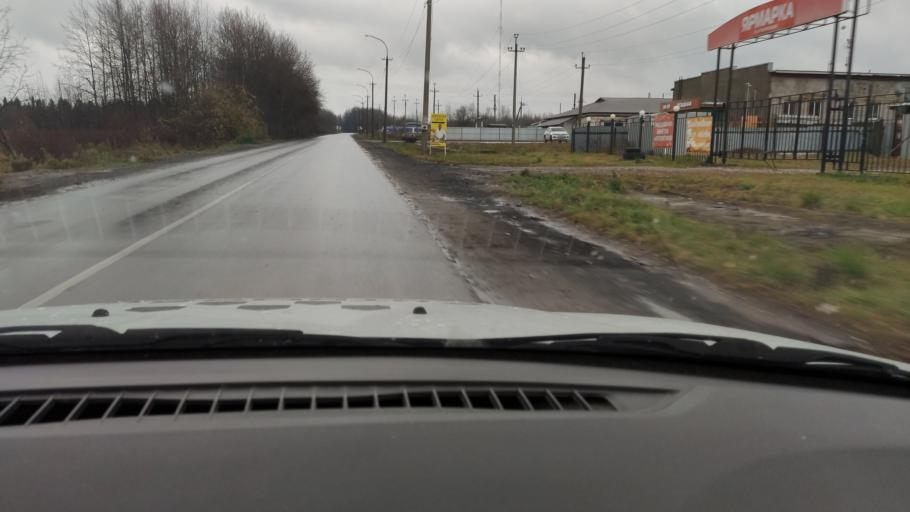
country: RU
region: Perm
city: Sylva
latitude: 58.0292
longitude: 56.7401
